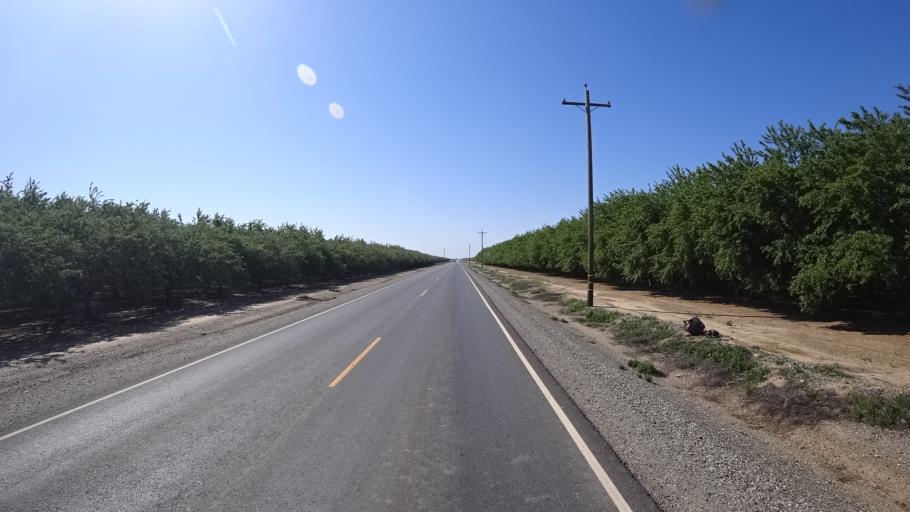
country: US
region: California
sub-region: Glenn County
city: Hamilton City
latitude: 39.6548
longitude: -122.0650
